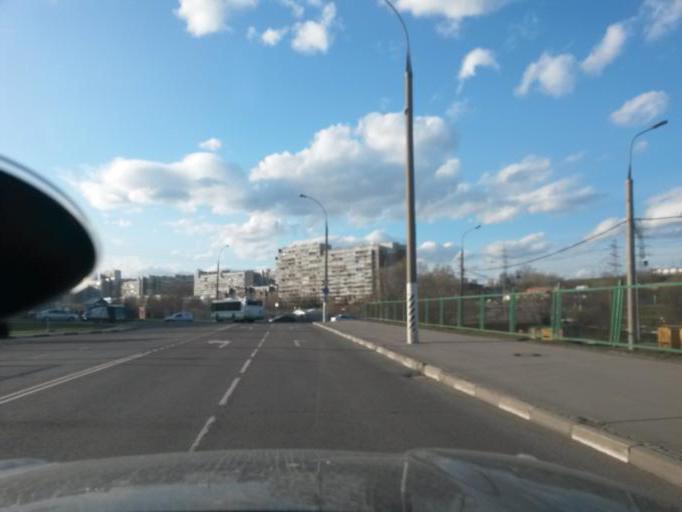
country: RU
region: Moscow
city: Annino
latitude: 55.5691
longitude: 37.5932
